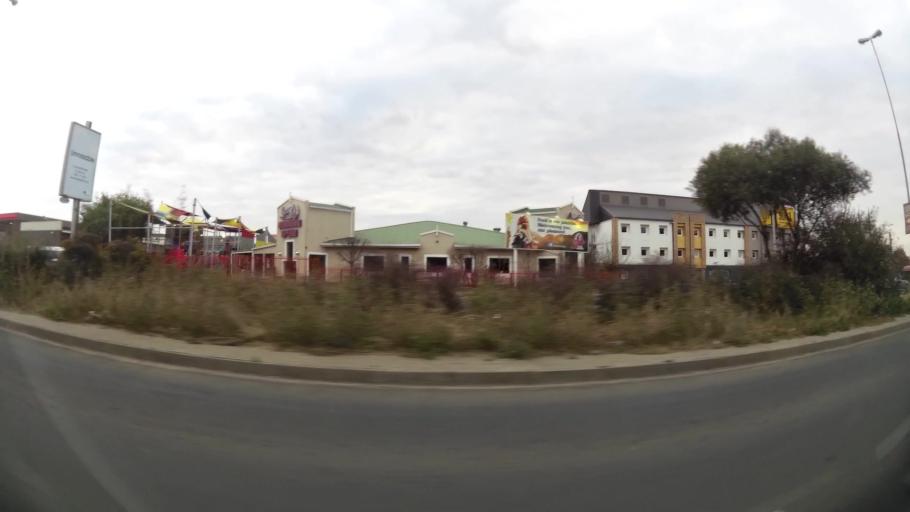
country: ZA
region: Orange Free State
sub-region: Mangaung Metropolitan Municipality
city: Bloemfontein
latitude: -29.1057
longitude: 26.1900
